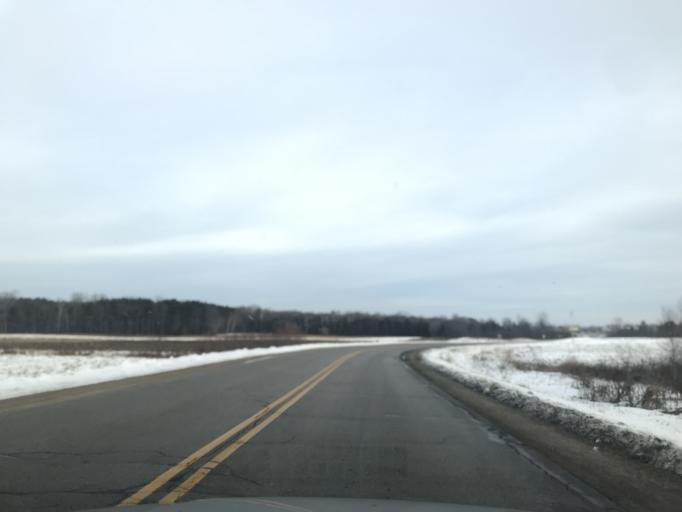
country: US
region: Wisconsin
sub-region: Brown County
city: Suamico
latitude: 44.6779
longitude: -88.0541
